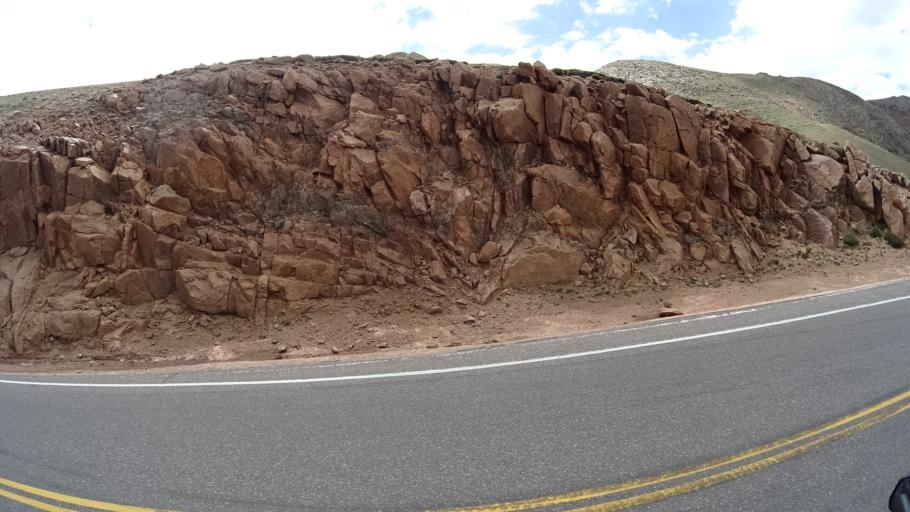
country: US
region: Colorado
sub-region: El Paso County
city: Cascade-Chipita Park
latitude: 38.8697
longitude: -105.0675
